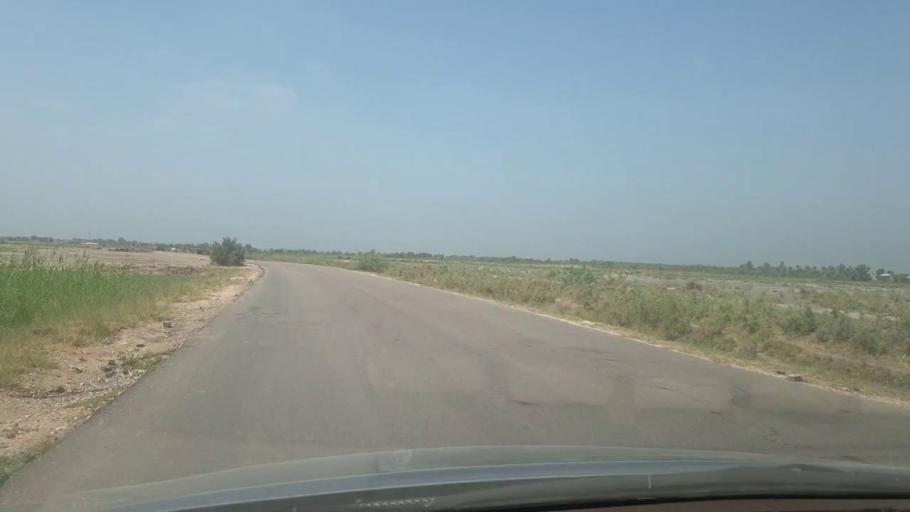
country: PK
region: Sindh
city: Ranipur
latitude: 27.2395
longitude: 68.5727
